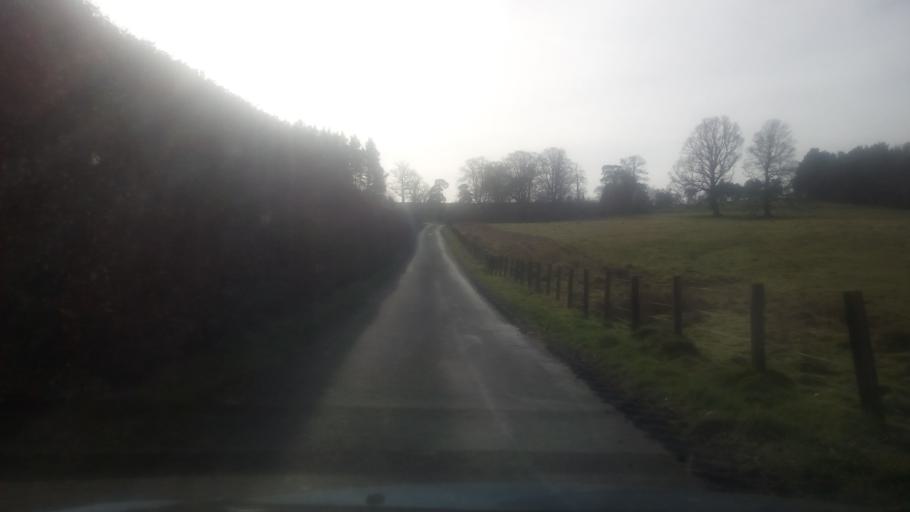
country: GB
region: Scotland
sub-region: The Scottish Borders
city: Jedburgh
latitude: 55.4435
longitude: -2.6423
